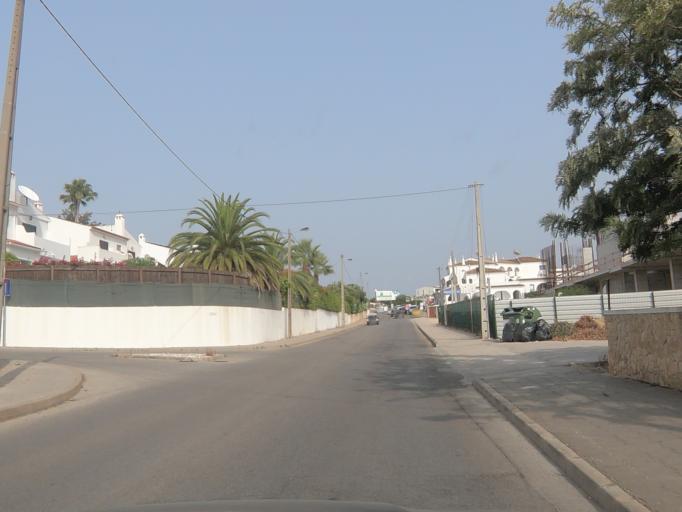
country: PT
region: Faro
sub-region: Albufeira
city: Guia
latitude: 37.0799
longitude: -8.3018
